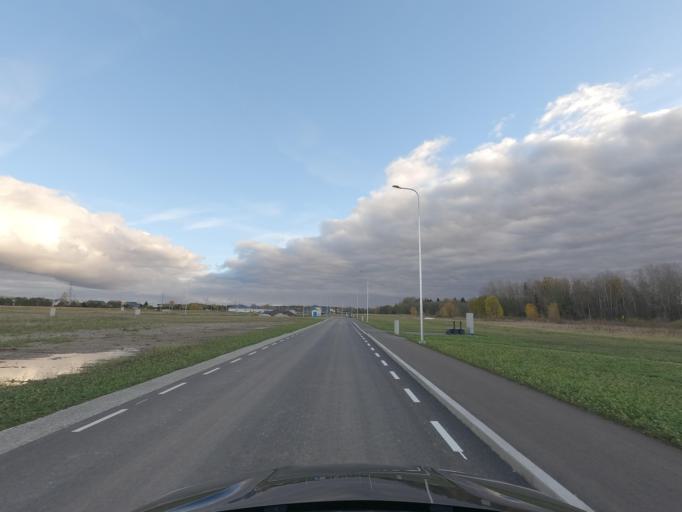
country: EE
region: Harju
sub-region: Saue linn
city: Saue
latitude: 59.3660
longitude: 24.5680
